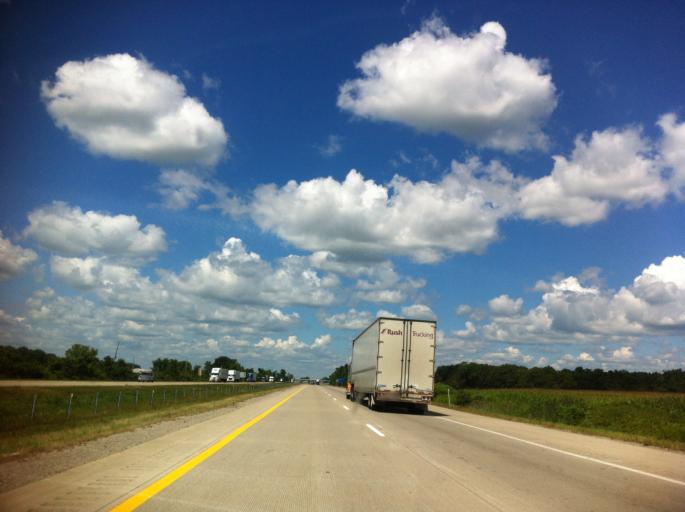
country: US
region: Ohio
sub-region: Lucas County
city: Sylvania
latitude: 41.7569
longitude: -83.6945
